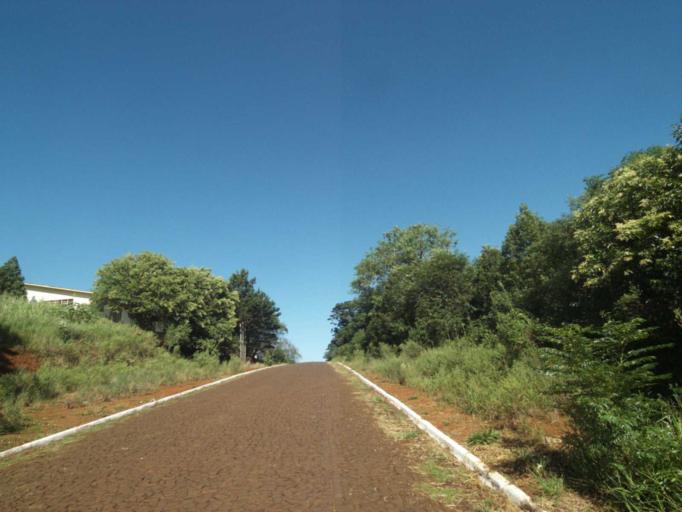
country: BR
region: Parana
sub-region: Laranjeiras Do Sul
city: Laranjeiras do Sul
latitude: -25.3827
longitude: -52.2019
